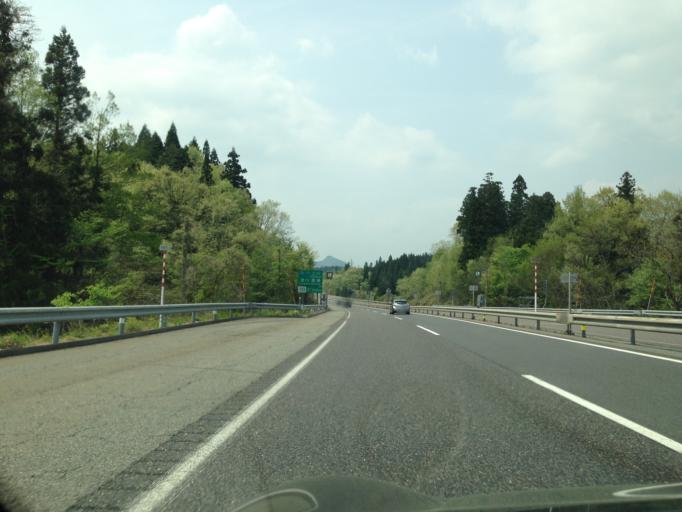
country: JP
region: Niigata
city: Muramatsu
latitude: 37.6695
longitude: 139.4595
